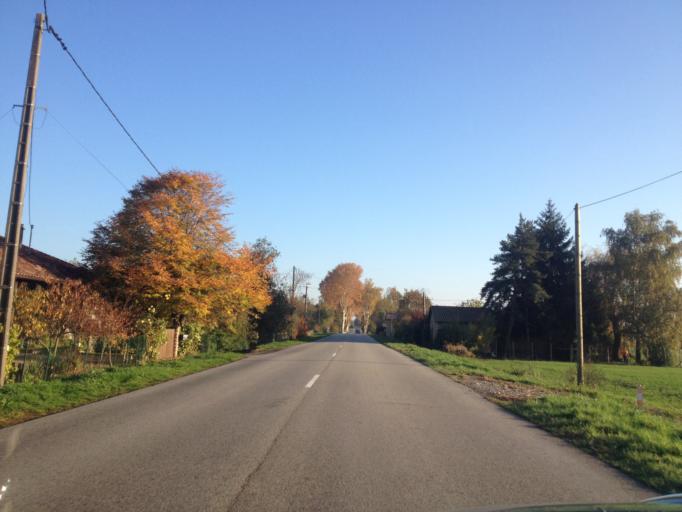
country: FR
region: Rhone-Alpes
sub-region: Departement de l'Ain
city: Saint-Jean-sur-Veyle
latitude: 46.2082
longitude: 4.9355
